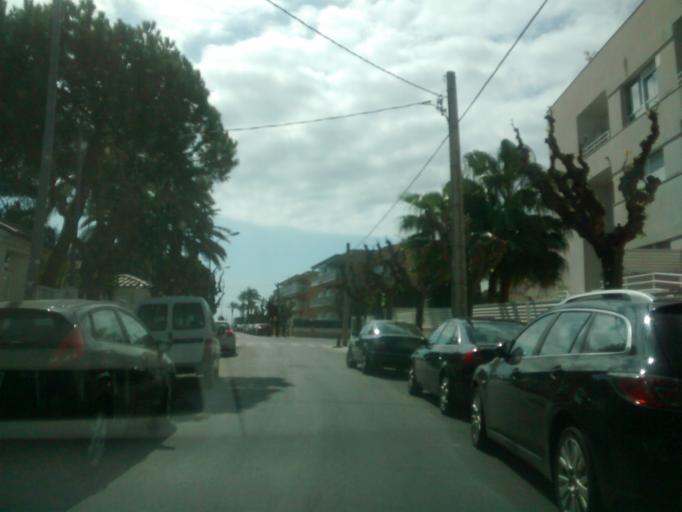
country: ES
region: Catalonia
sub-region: Provincia de Barcelona
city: Cubelles
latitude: 41.2041
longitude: 1.6807
